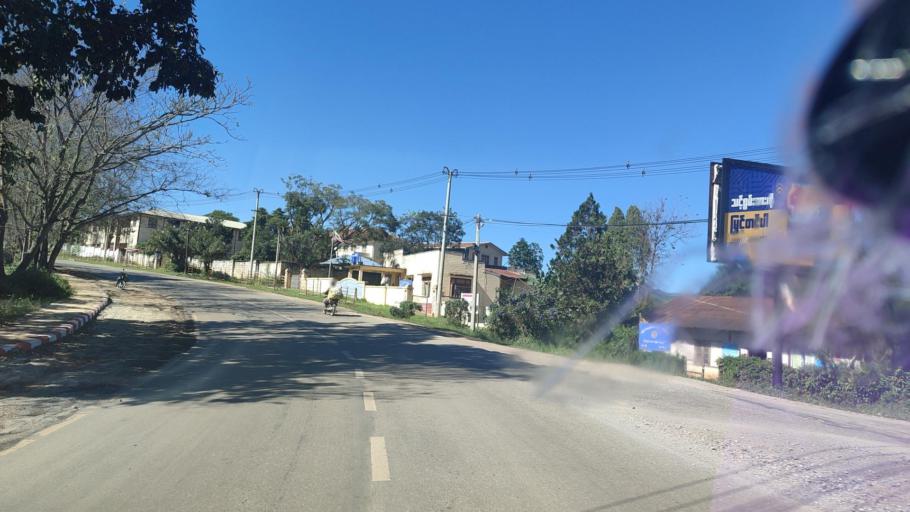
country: MM
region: Shan
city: Taunggyi
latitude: 20.9193
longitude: 97.5638
